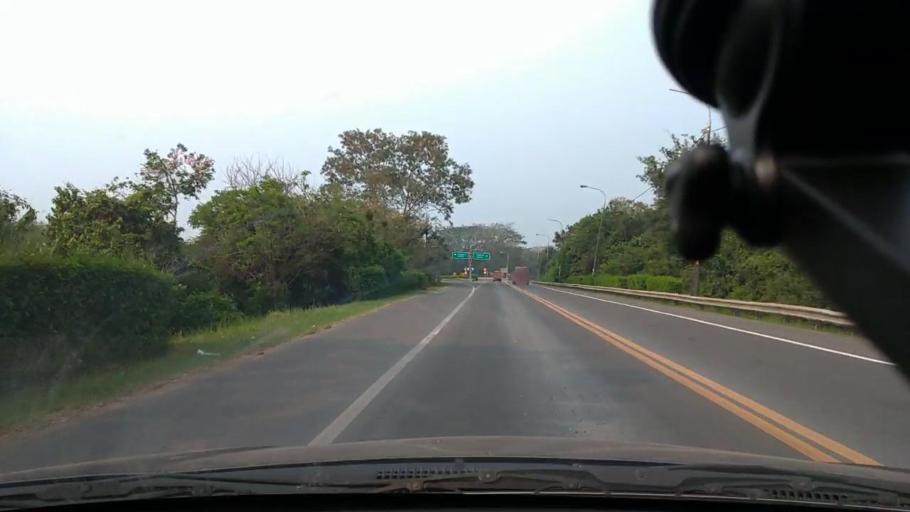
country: ID
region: Banten
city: Serang
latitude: -6.0903
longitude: 106.1424
